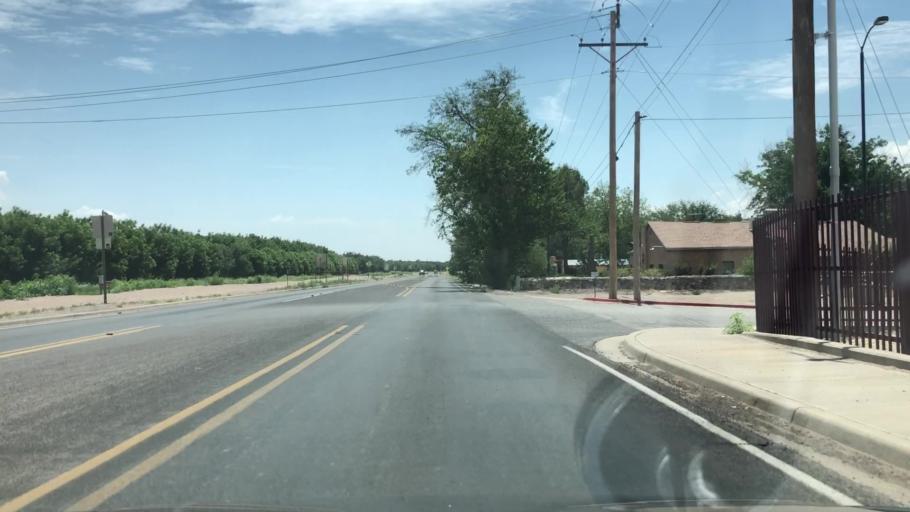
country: US
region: New Mexico
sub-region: Dona Ana County
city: La Union
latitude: 31.9972
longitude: -106.6552
